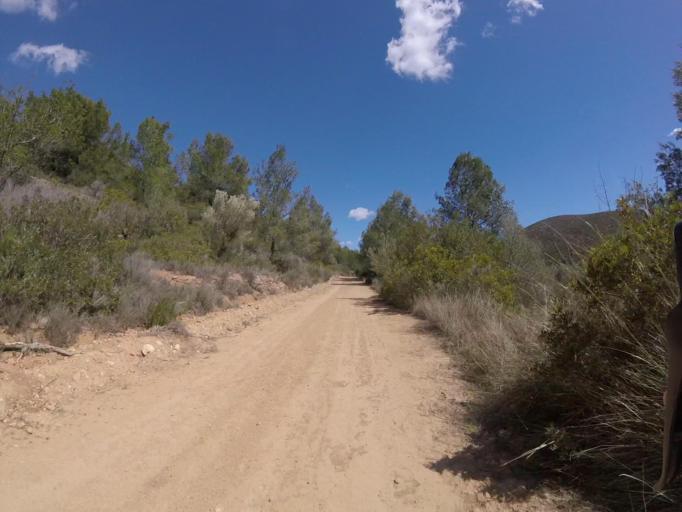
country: ES
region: Valencia
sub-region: Provincia de Castello
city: Cabanes
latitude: 40.1608
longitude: 0.1099
